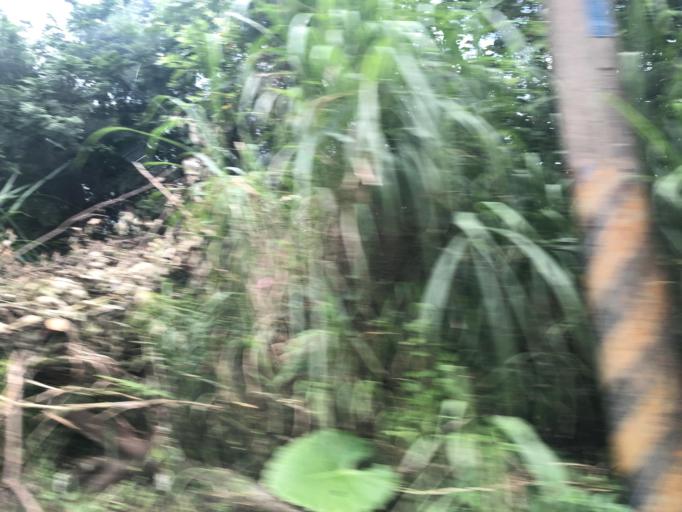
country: TW
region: Taiwan
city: Daxi
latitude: 24.8760
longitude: 121.4161
